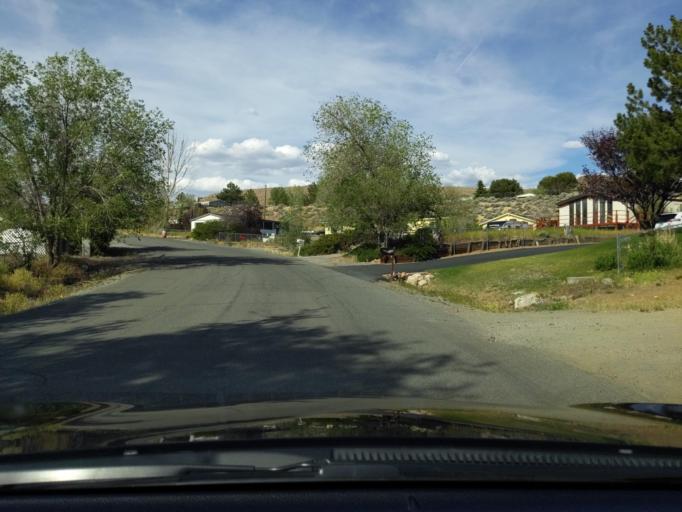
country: US
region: Nevada
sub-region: Washoe County
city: Sun Valley
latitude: 39.5812
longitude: -119.7722
